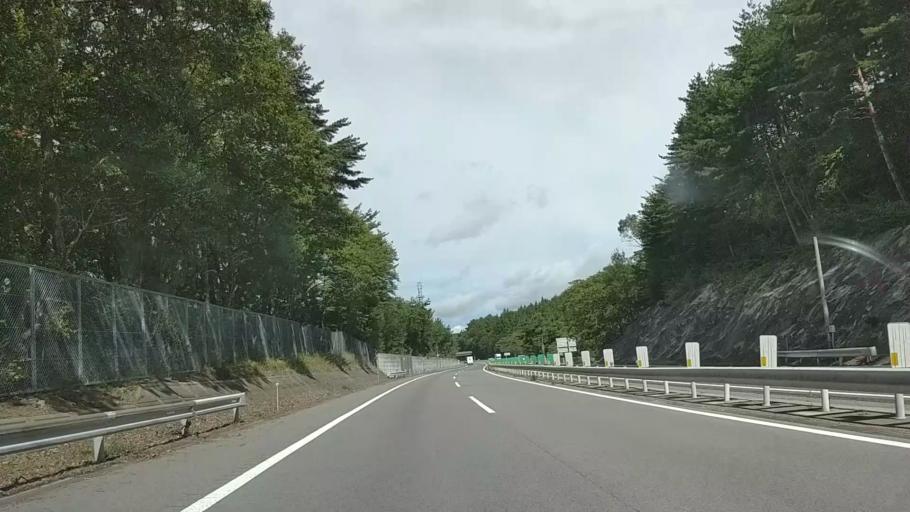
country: JP
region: Nagano
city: Chino
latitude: 35.8744
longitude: 138.3060
